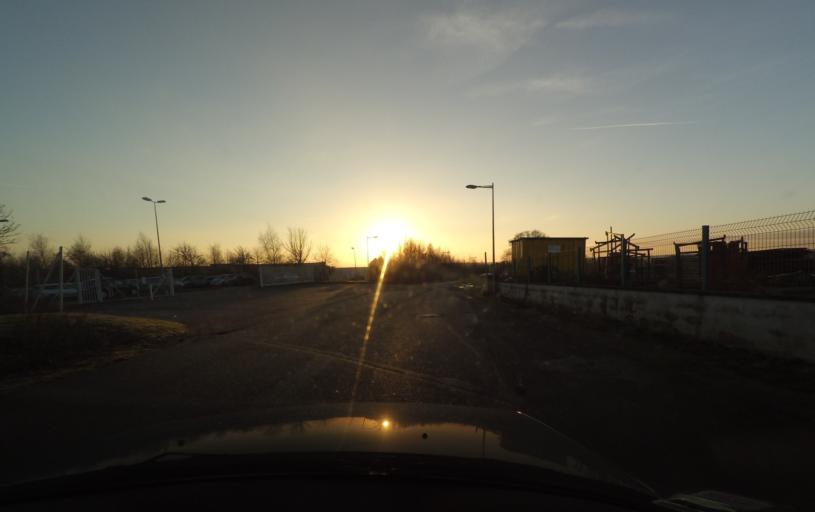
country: FR
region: Pays de la Loire
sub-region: Departement de la Mayenne
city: Villaines-la-Juhel
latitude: 48.3371
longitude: -0.2772
